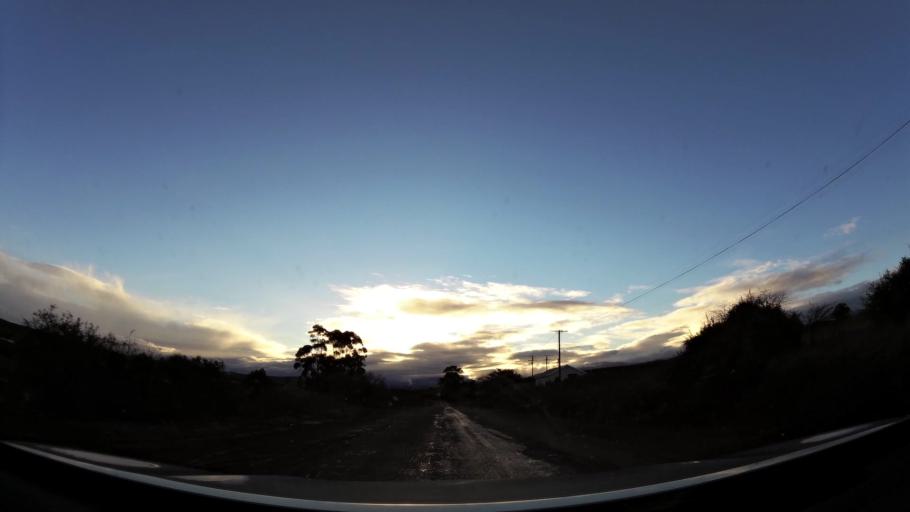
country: ZA
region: Western Cape
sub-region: Eden District Municipality
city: Riversdale
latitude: -34.0807
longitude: 20.9319
